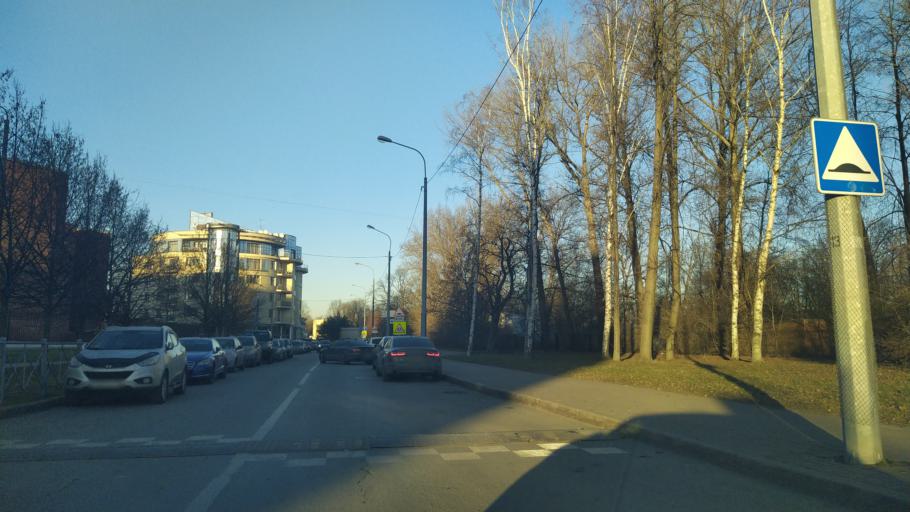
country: RU
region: St.-Petersburg
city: Novaya Derevnya
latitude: 59.9724
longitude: 30.2763
